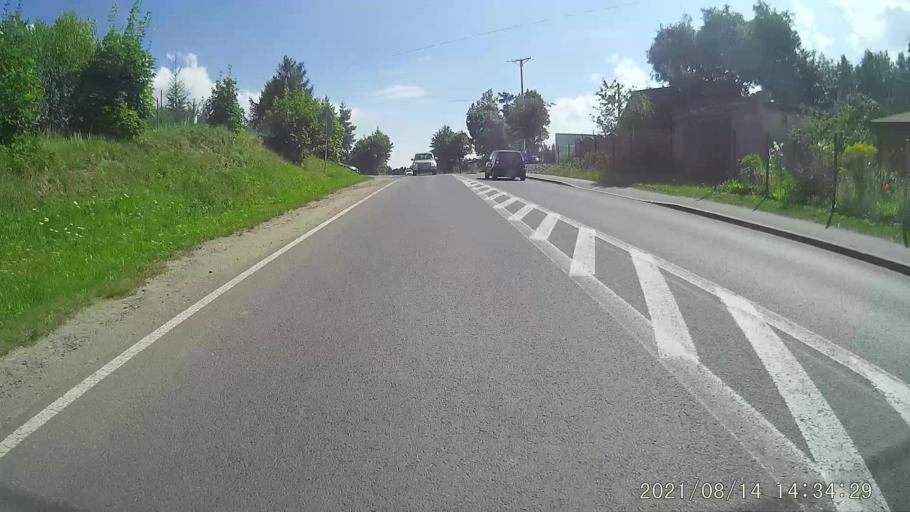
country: PL
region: Lower Silesian Voivodeship
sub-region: Powiat klodzki
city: Nowa Ruda
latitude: 50.5662
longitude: 16.5338
